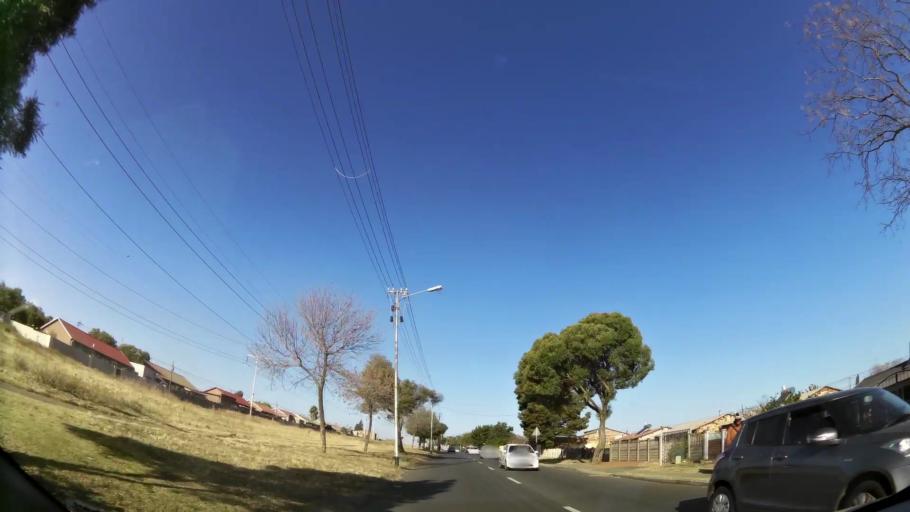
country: ZA
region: Gauteng
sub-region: City of Johannesburg Metropolitan Municipality
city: Johannesburg
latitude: -26.2138
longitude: 27.9792
